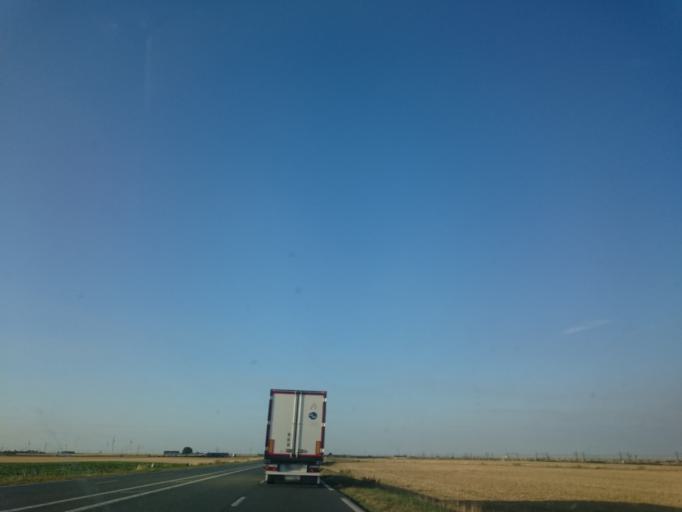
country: FR
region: Centre
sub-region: Departement du Loiret
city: Artenay
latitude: 48.1018
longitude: 1.8875
